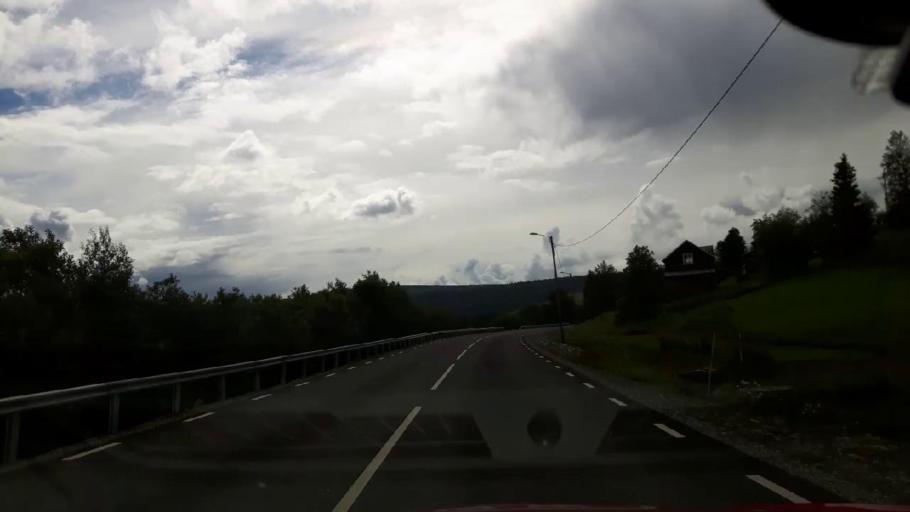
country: NO
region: Nord-Trondelag
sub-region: Royrvik
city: Royrvik
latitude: 64.8042
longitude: 14.0715
